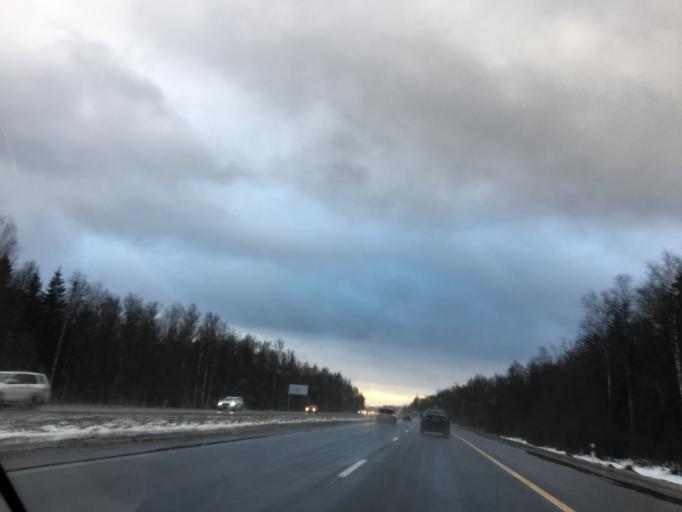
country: RU
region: Moskovskaya
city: Danki
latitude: 54.9907
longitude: 37.5380
